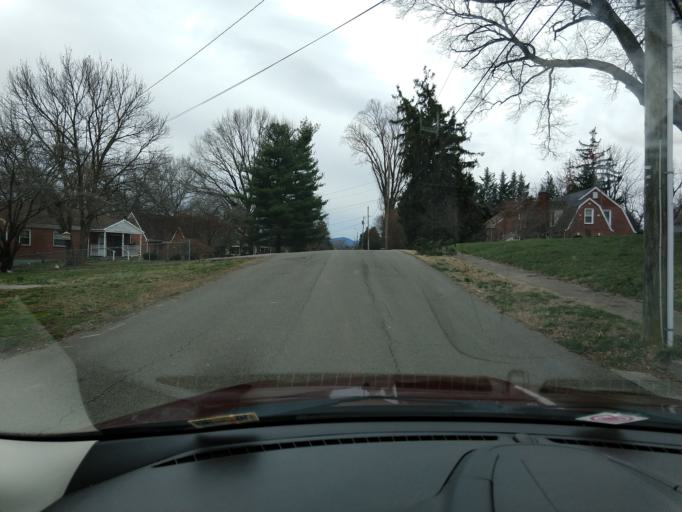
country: US
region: Virginia
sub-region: City of Roanoke
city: Roanoke
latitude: 37.3038
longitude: -79.9385
